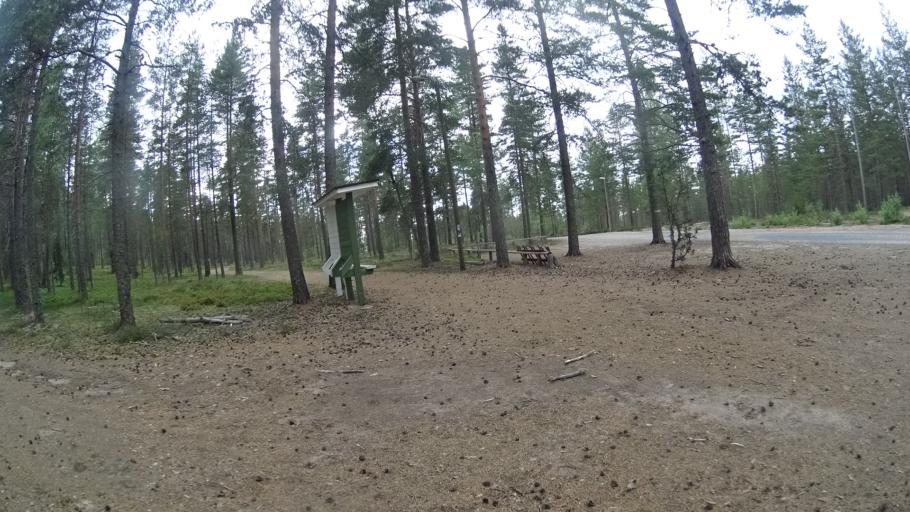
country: FI
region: Satakunta
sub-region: Pohjois-Satakunta
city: Jaemijaervi
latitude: 61.7758
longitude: 22.7309
